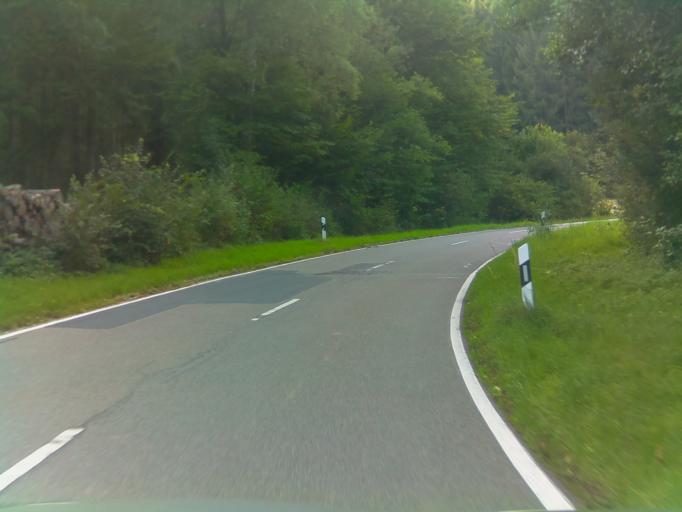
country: DE
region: Hesse
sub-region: Regierungsbezirk Darmstadt
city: Rothenberg
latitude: 49.5549
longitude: 8.8973
